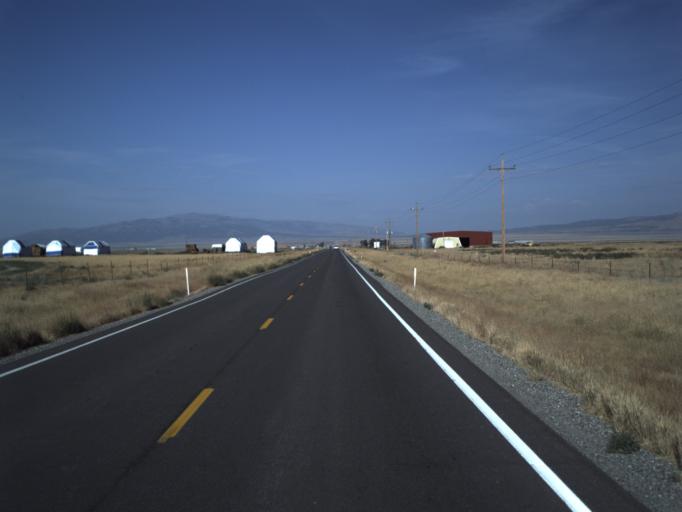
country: US
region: Idaho
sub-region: Oneida County
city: Malad City
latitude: 41.9670
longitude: -112.8680
